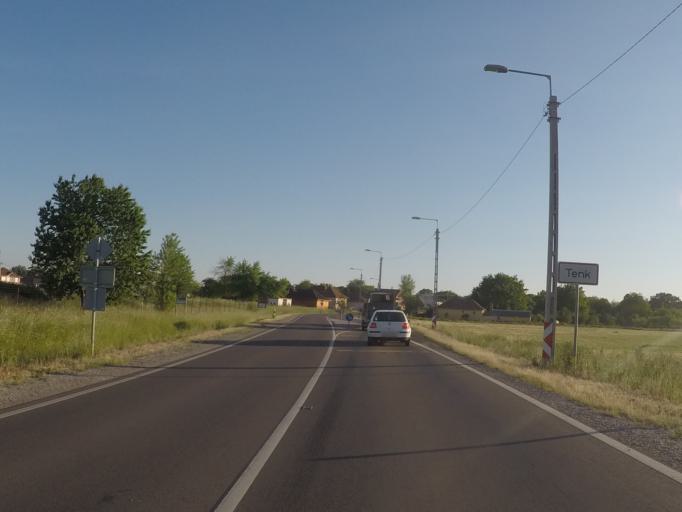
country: HU
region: Heves
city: Erdotelek
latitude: 47.6594
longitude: 20.3475
